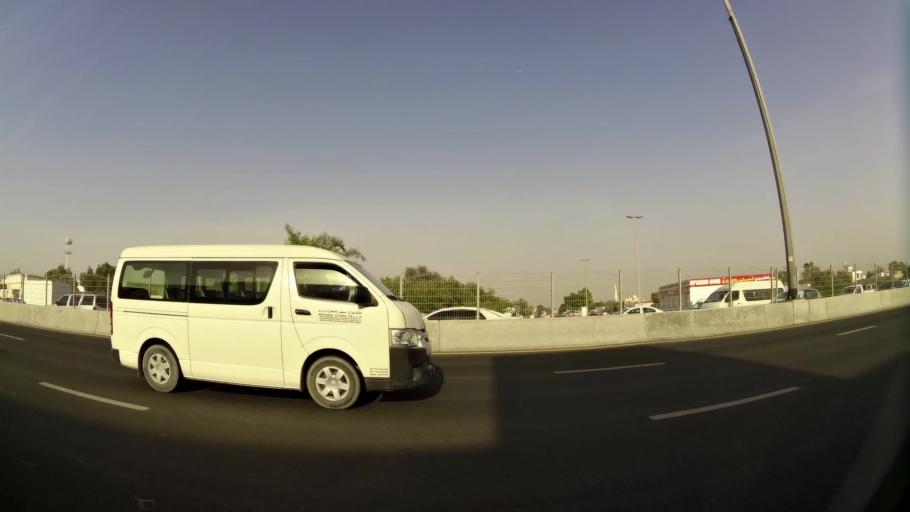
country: AE
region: Ash Shariqah
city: Sharjah
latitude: 25.2298
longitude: 55.3775
